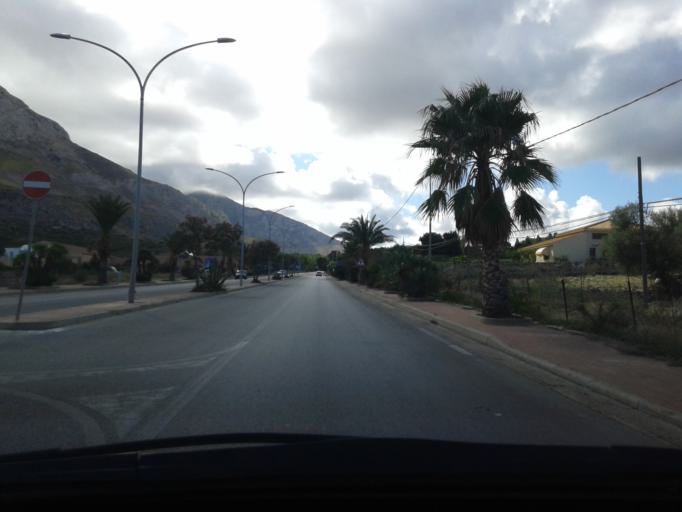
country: IT
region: Sicily
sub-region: Trapani
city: San Vito Lo Capo
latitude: 38.1615
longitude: 12.7367
